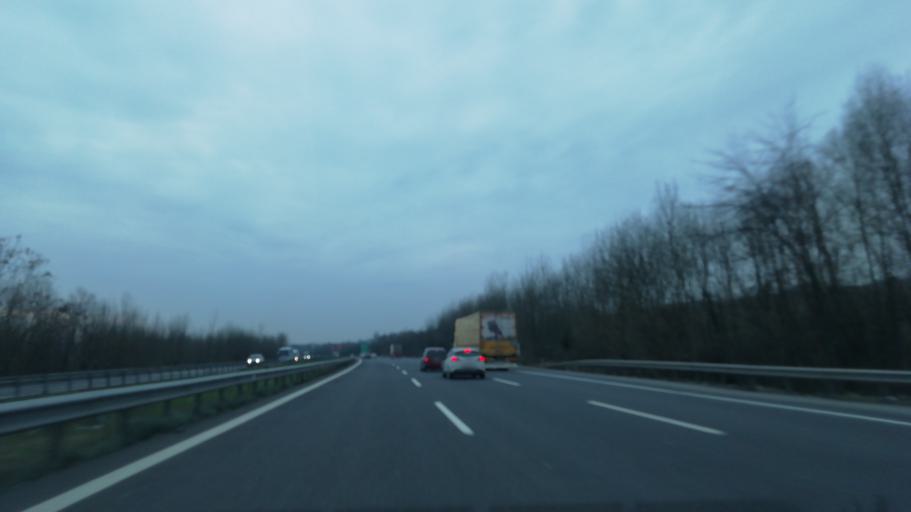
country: TR
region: Sakarya
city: Karadere
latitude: 40.7862
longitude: 30.8165
